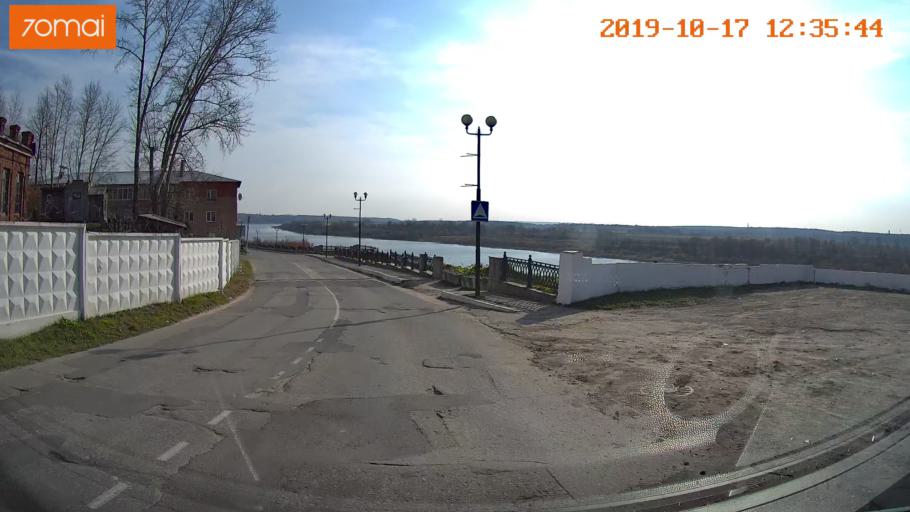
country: RU
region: Rjazan
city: Kasimov
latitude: 54.9420
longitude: 41.3708
